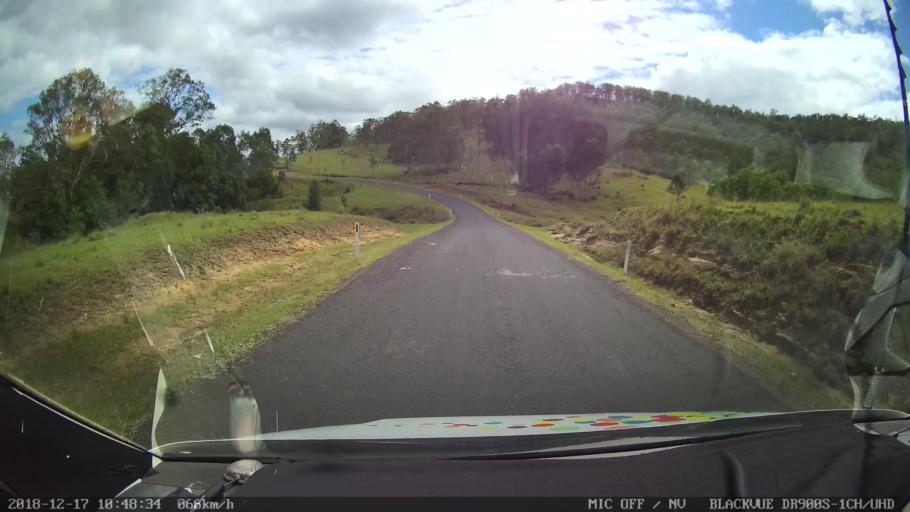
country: AU
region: New South Wales
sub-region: Clarence Valley
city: Gordon
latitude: -28.8720
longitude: 152.5713
